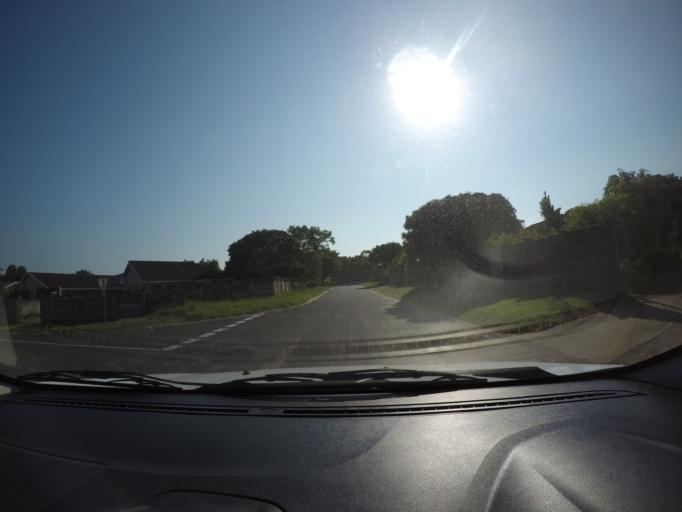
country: ZA
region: KwaZulu-Natal
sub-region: uThungulu District Municipality
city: Richards Bay
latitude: -28.7149
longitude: 32.0324
